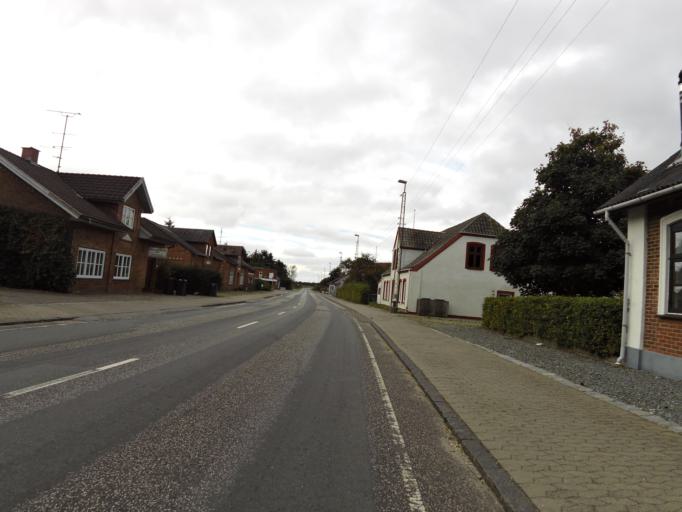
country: DK
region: South Denmark
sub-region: Tonder Kommune
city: Sherrebek
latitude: 55.2152
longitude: 8.8302
